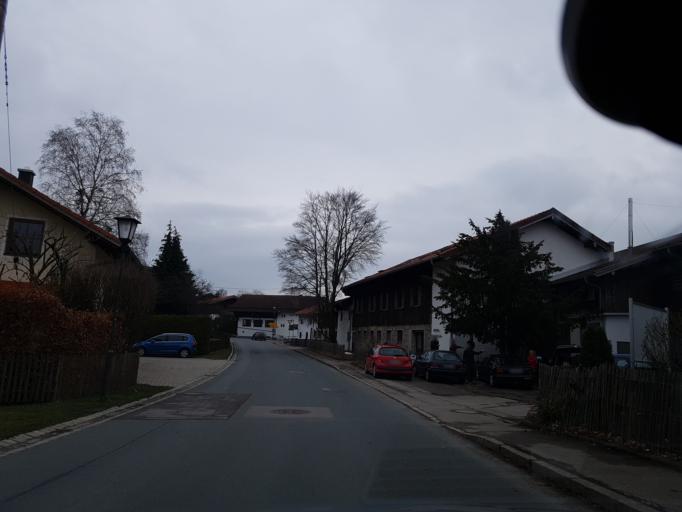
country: DE
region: Bavaria
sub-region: Upper Bavaria
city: Bruckmuhl
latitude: 47.9277
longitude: 11.8957
